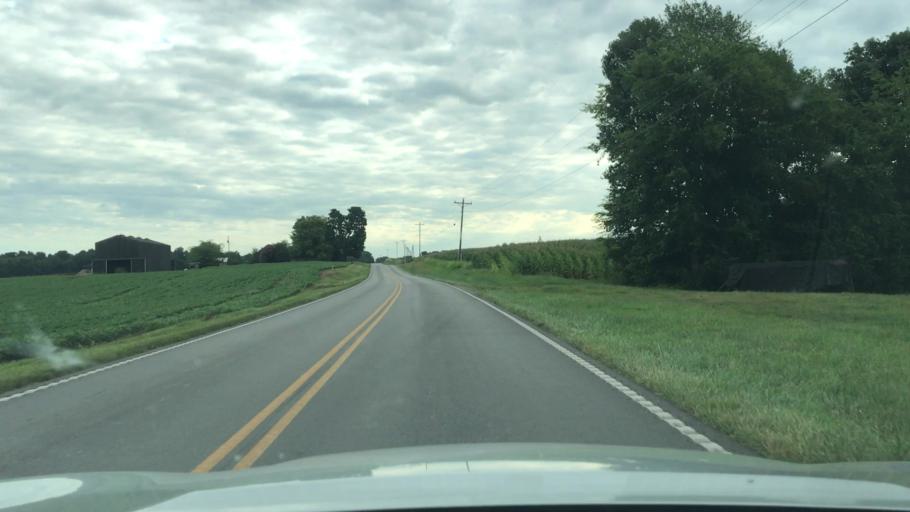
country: US
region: Kentucky
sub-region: Todd County
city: Elkton
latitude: 36.7428
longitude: -87.1792
